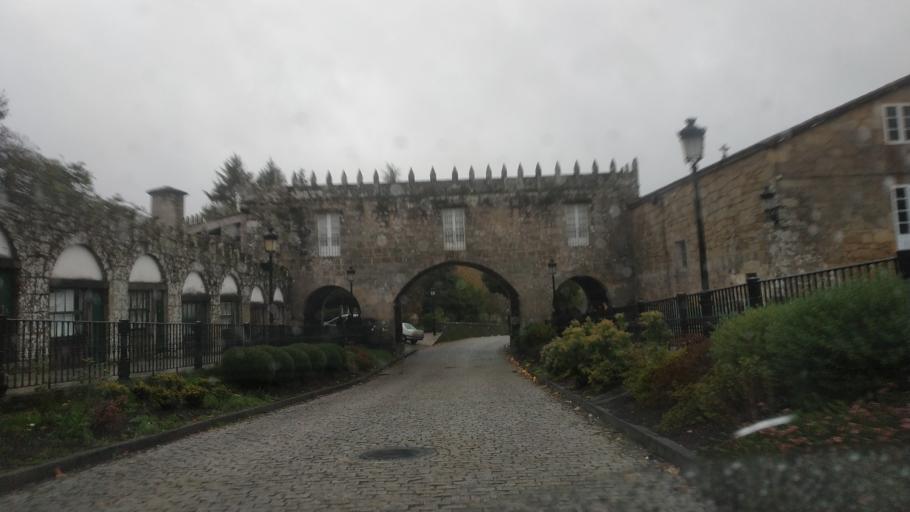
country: ES
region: Galicia
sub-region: Provincia da Coruna
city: Negreira
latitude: 42.9079
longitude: -8.7384
